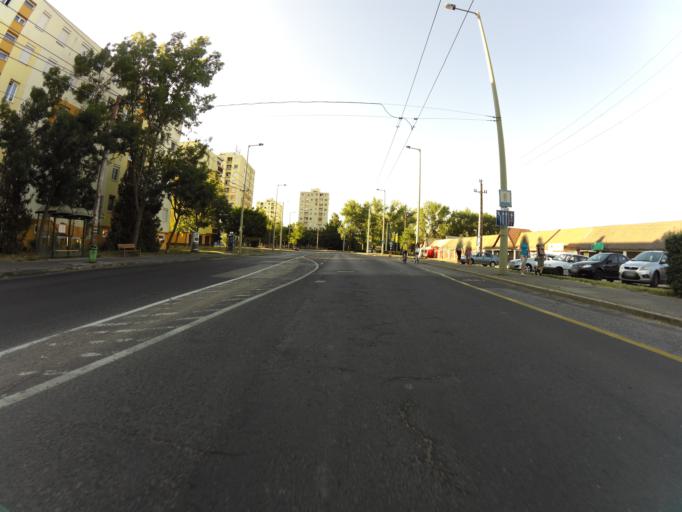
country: HU
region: Csongrad
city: Szeged
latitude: 46.2606
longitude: 20.1713
